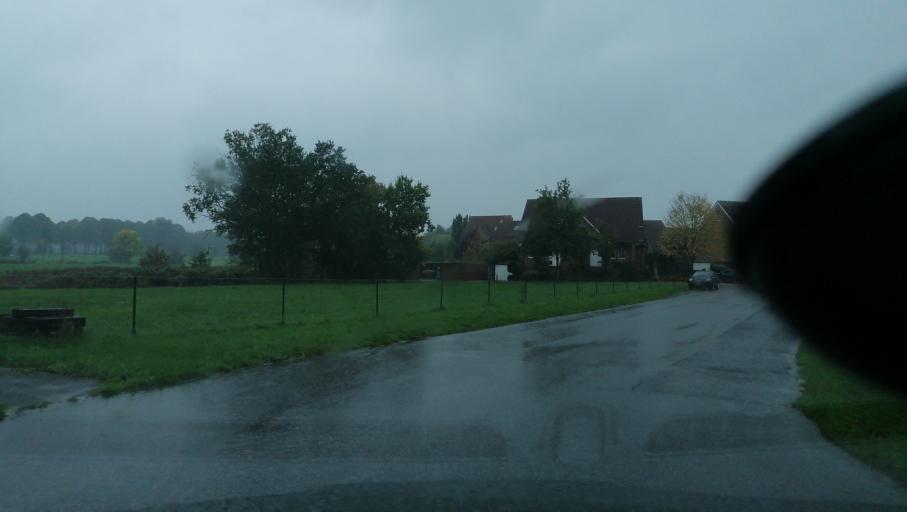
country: DE
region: North Rhine-Westphalia
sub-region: Regierungsbezirk Munster
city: Recklinghausen
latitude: 51.5879
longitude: 7.1770
